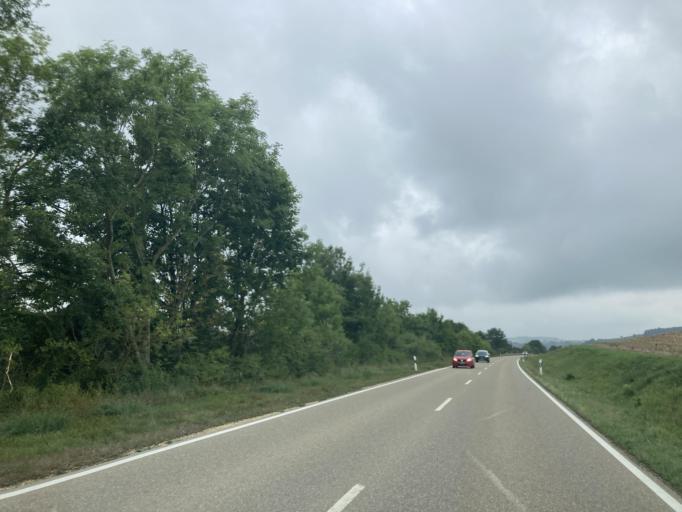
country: DE
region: Baden-Wuerttemberg
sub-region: Regierungsbezirk Stuttgart
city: Dischingen
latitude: 48.7025
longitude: 10.3690
